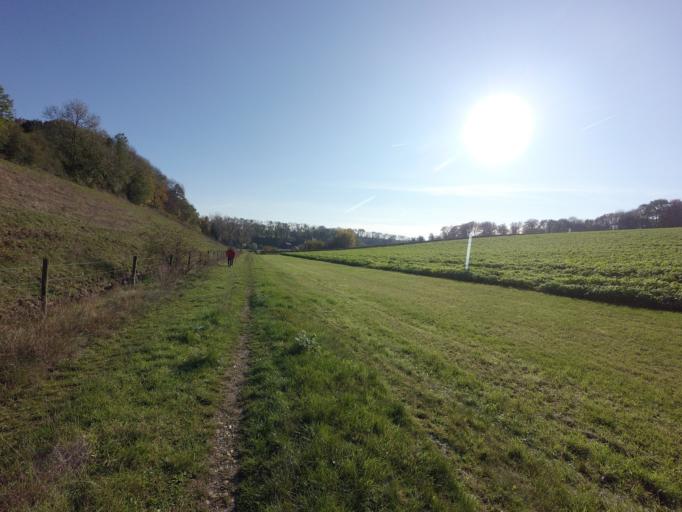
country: NL
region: Limburg
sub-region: Gemeente Voerendaal
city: Ubachsberg
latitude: 50.8302
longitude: 5.9563
